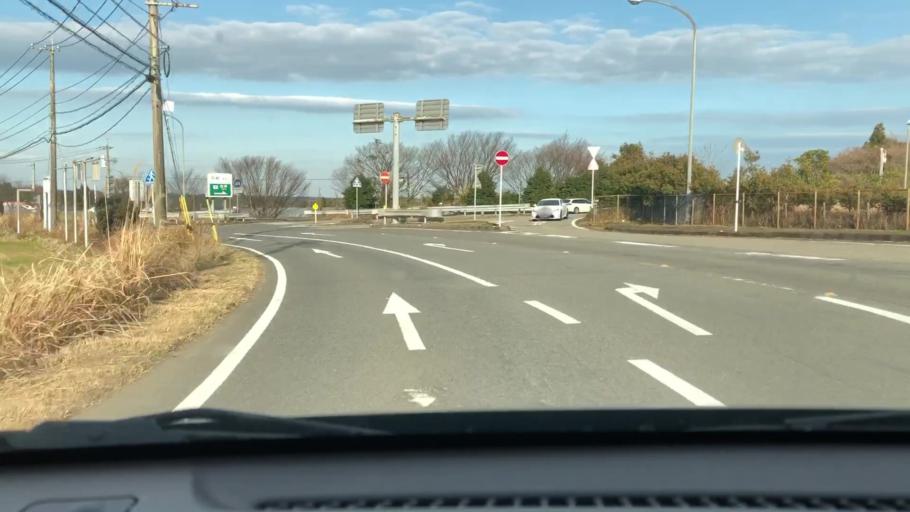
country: JP
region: Miyazaki
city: Miyazaki-shi
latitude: 31.8212
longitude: 131.2975
